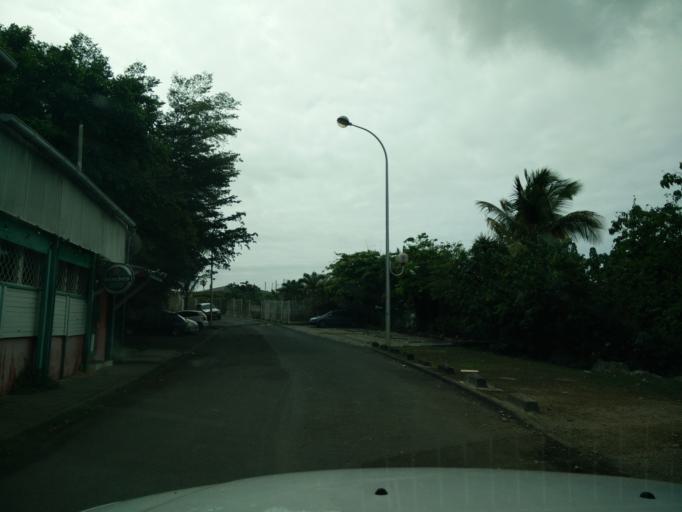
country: GP
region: Guadeloupe
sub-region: Guadeloupe
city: Pointe-a-Pitre
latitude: 16.2194
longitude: -61.5269
